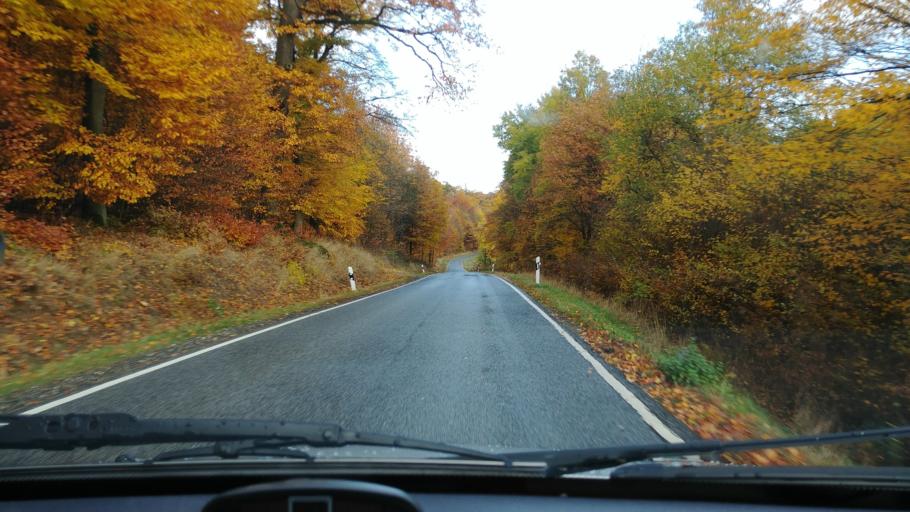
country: DE
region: Hesse
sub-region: Regierungsbezirk Darmstadt
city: Idstein
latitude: 50.2009
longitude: 8.2428
